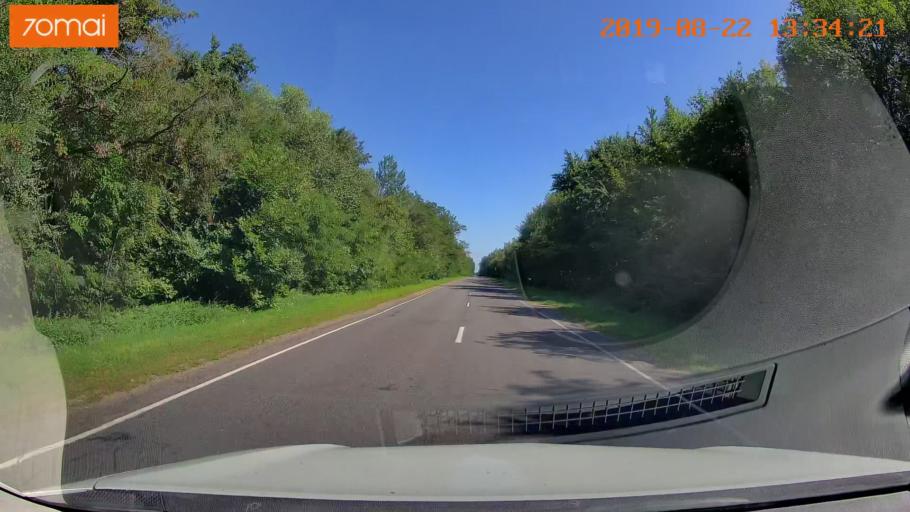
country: BY
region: Minsk
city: Staryya Darohi
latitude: 53.2154
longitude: 28.2394
